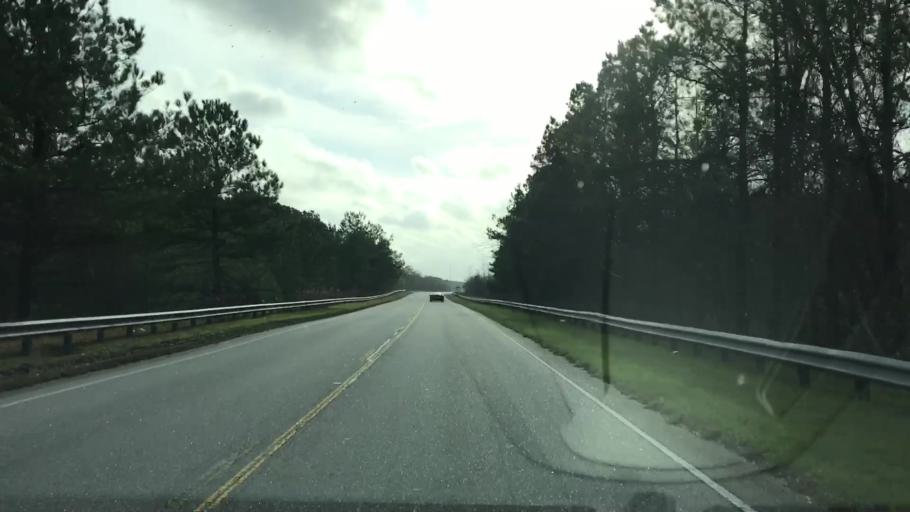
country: US
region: South Carolina
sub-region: Williamsburg County
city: Andrews
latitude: 33.3126
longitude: -79.6715
